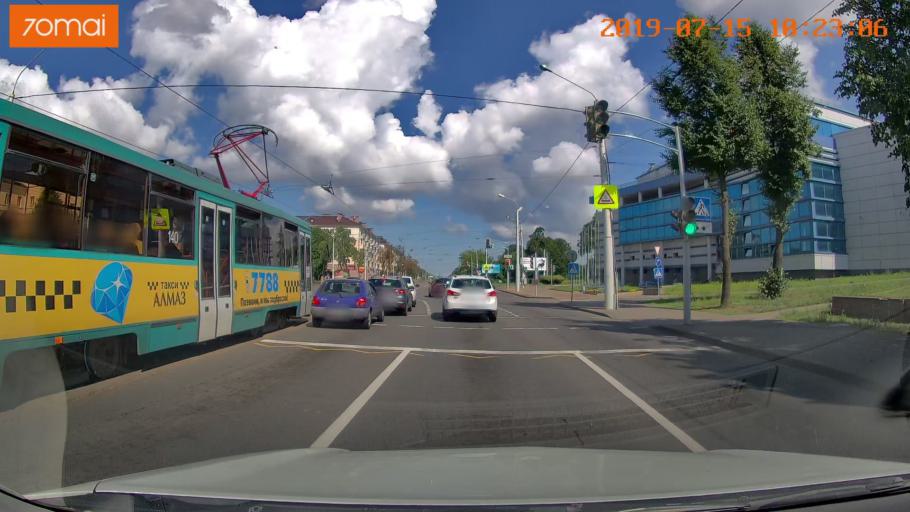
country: BY
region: Minsk
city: Minsk
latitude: 53.8866
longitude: 27.6185
